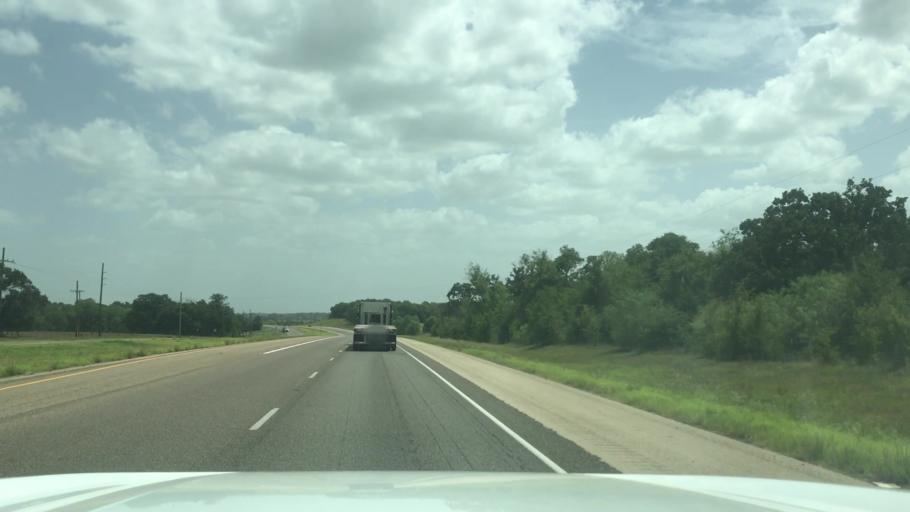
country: US
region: Texas
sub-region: Robertson County
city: Calvert
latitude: 31.0288
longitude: -96.7094
